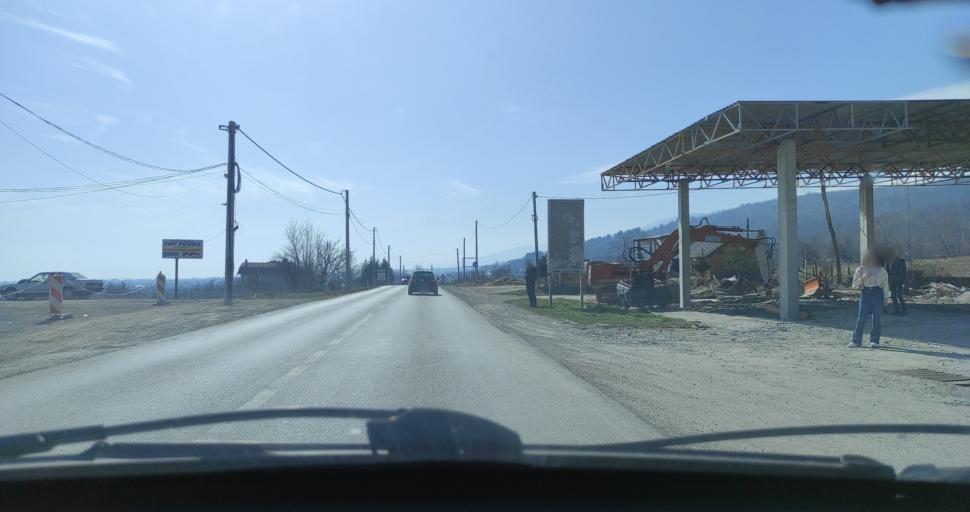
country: XK
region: Gjakova
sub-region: Komuna e Decanit
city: Strellc i Eperm
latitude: 42.5739
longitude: 20.2941
